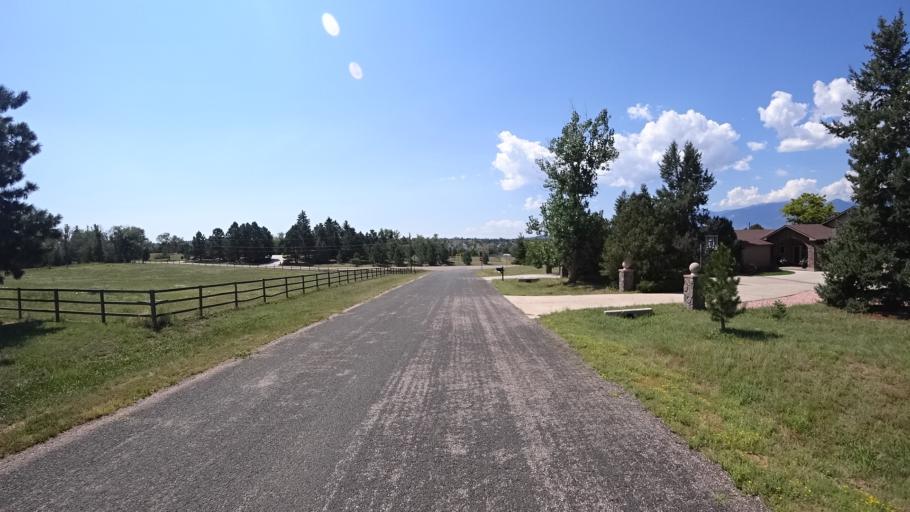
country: US
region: Colorado
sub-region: El Paso County
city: Air Force Academy
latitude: 38.9365
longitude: -104.7817
